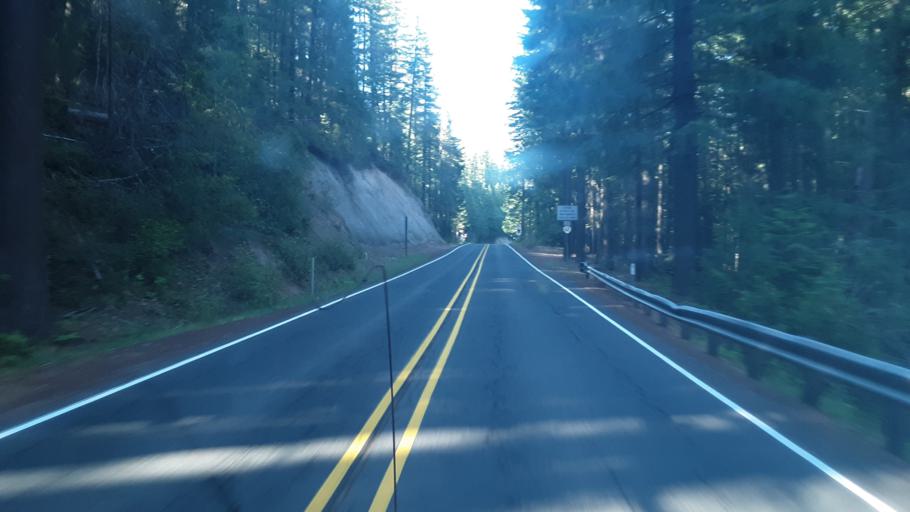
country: US
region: Oregon
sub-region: Jackson County
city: Shady Cove
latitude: 42.9235
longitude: -122.4283
